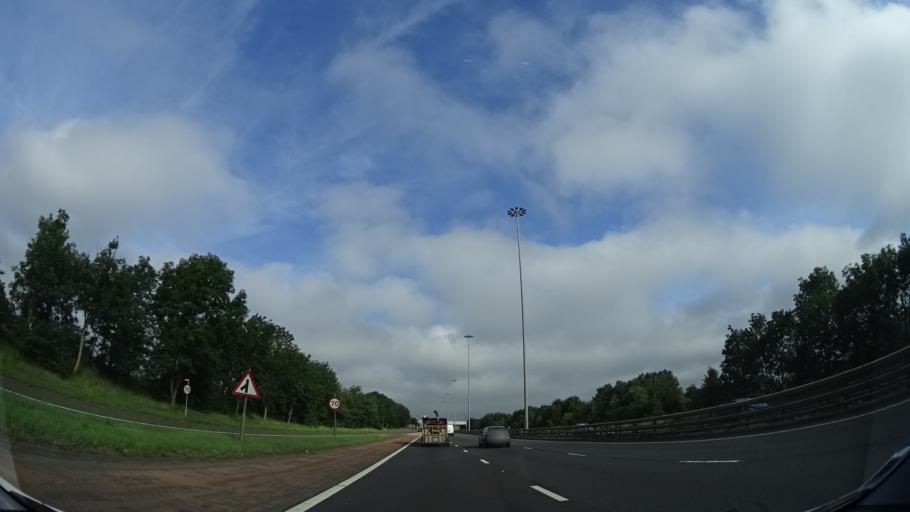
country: GB
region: Scotland
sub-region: Renfrewshire
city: Renfrew
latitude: 55.8567
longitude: -4.3461
